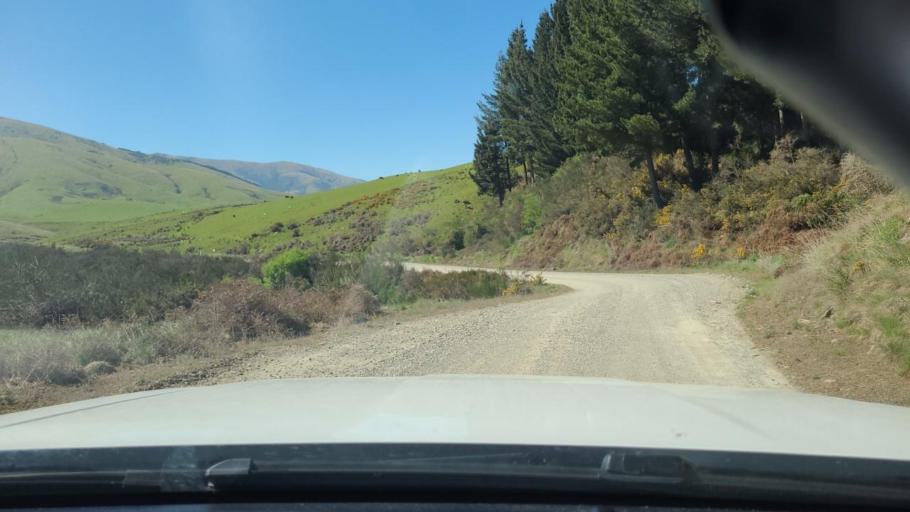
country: NZ
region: Southland
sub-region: Gore District
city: Gore
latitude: -45.7462
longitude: 168.9048
